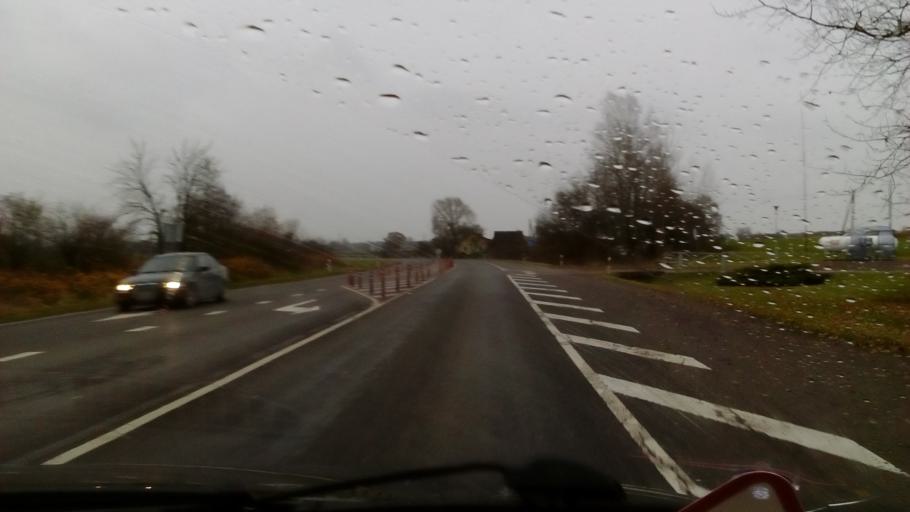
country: LT
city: Simnas
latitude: 54.5584
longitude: 23.6562
